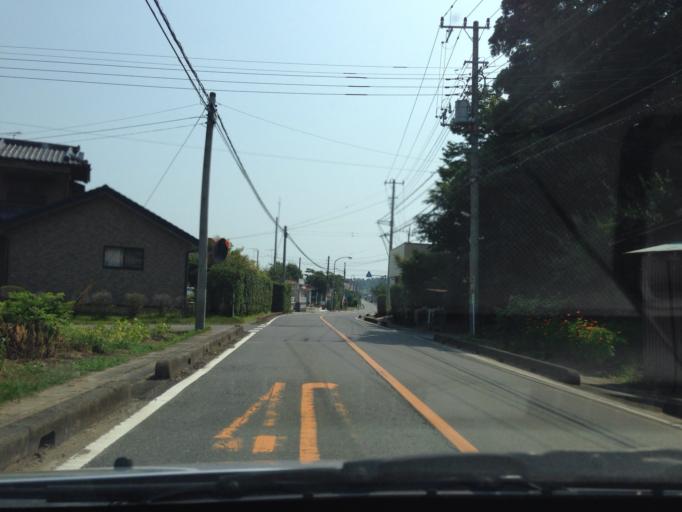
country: JP
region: Ibaraki
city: Inashiki
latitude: 36.0113
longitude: 140.3478
